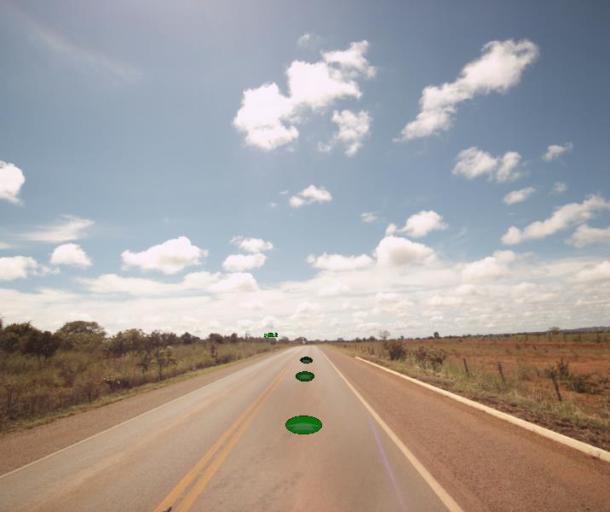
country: BR
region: Goias
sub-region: Padre Bernardo
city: Padre Bernardo
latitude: -15.1513
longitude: -48.3484
